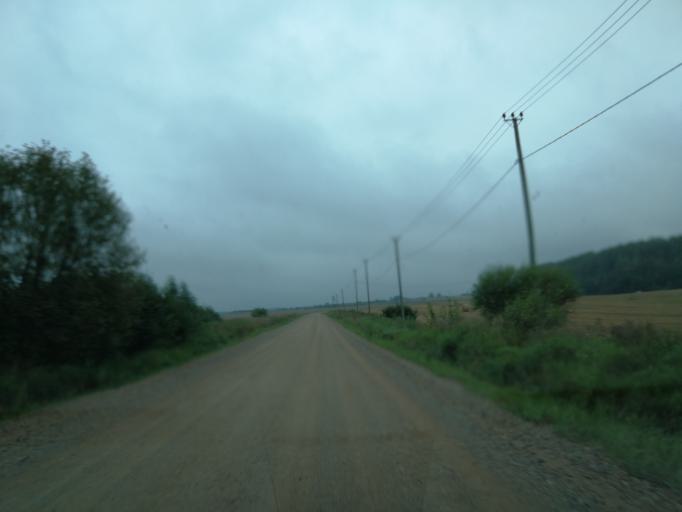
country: LV
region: Vilanu
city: Vilani
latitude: 56.3757
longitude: 27.0471
